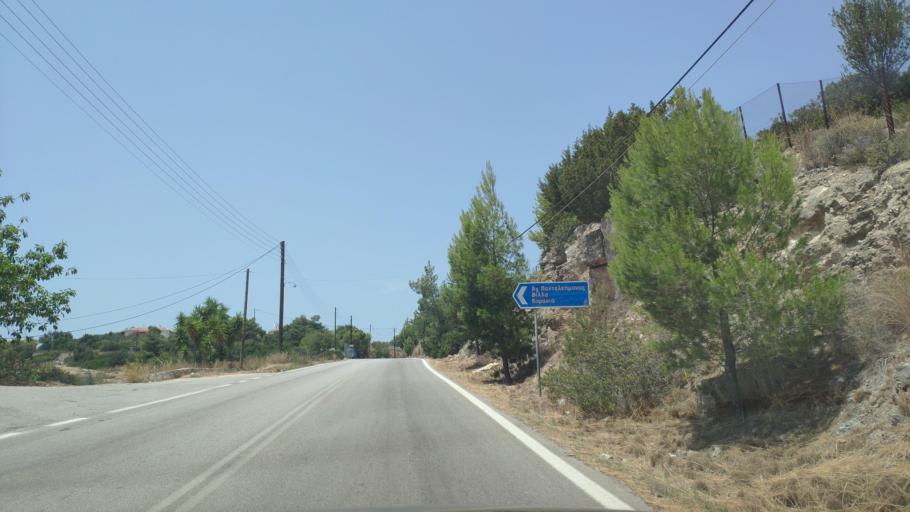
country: GR
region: Peloponnese
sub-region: Nomos Argolidos
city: Kranidi
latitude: 37.3743
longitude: 23.1510
